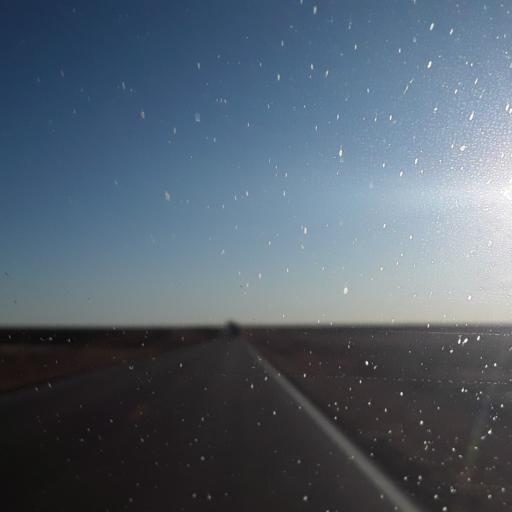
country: US
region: Kansas
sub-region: Wallace County
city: Sharon Springs
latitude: 39.1063
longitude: -101.7329
